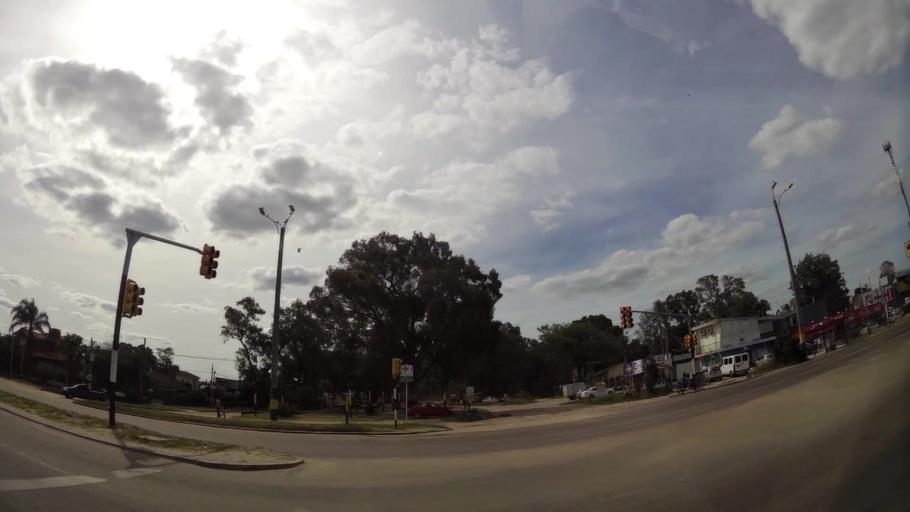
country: UY
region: Canelones
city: Barra de Carrasco
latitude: -34.8352
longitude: -55.9825
